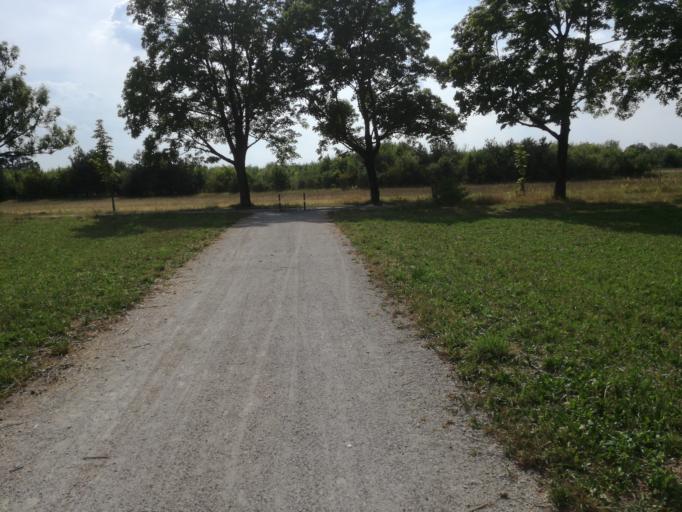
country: DE
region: Bavaria
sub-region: Upper Bavaria
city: Grafelfing
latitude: 48.1306
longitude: 11.4075
